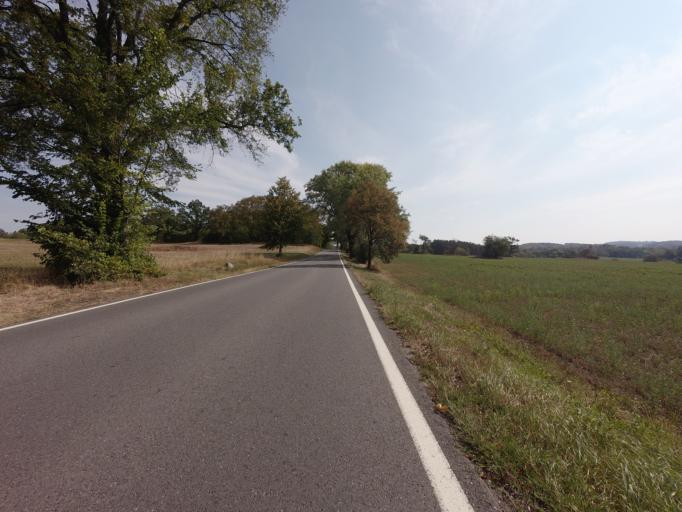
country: CZ
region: Central Bohemia
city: Petrovice
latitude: 49.5627
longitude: 14.3584
